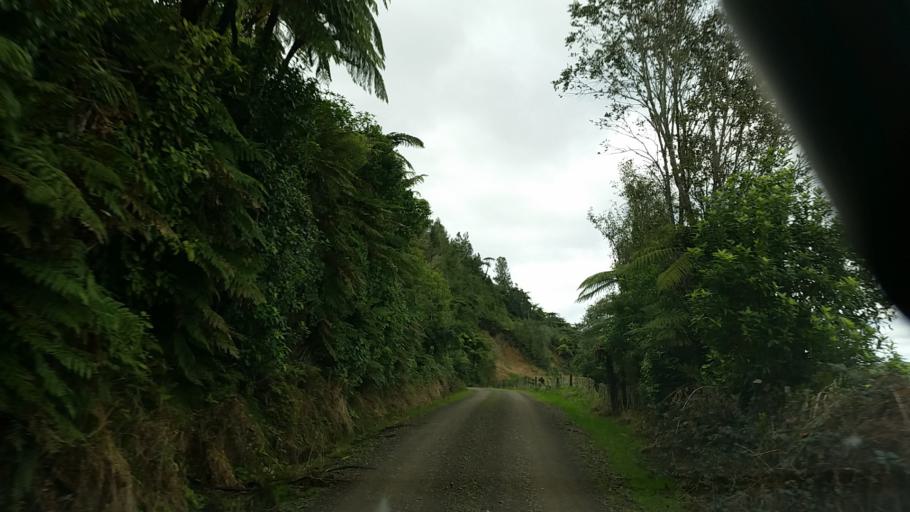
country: NZ
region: Taranaki
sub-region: New Plymouth District
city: Waitara
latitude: -39.0219
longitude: 174.5554
